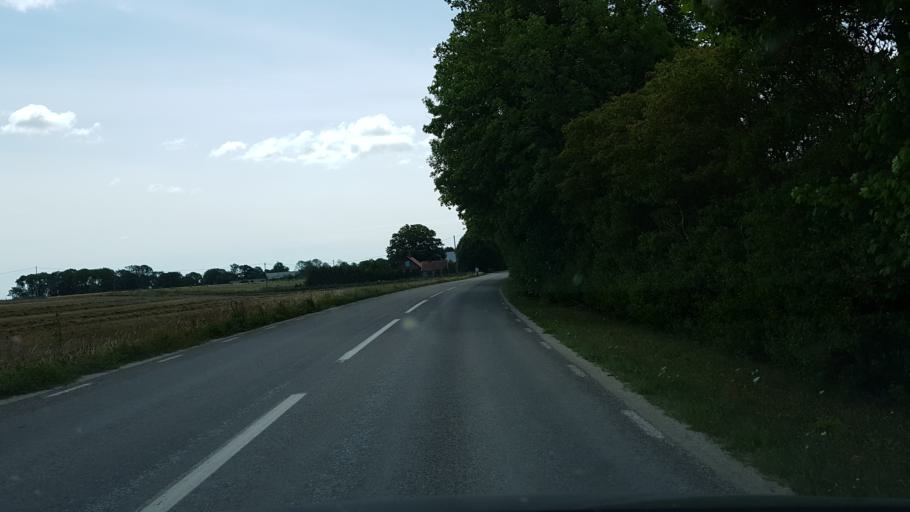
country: SE
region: Gotland
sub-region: Gotland
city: Visby
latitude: 57.7586
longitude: 18.4268
